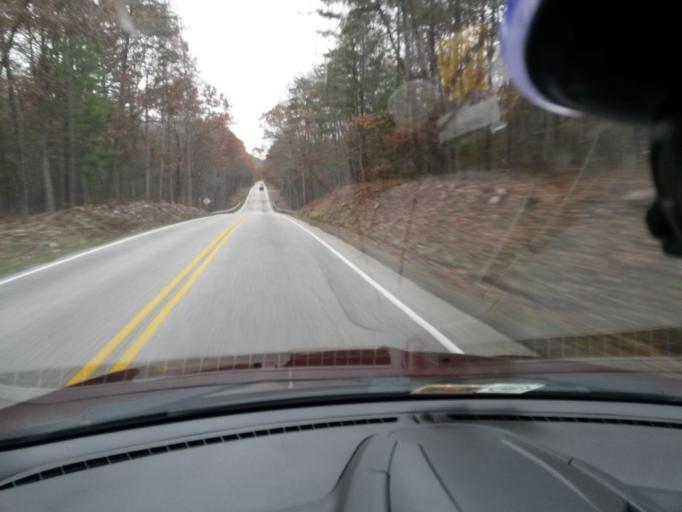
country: US
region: Virginia
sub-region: Rockbridge County
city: Glasgow
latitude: 37.6600
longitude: -79.4218
